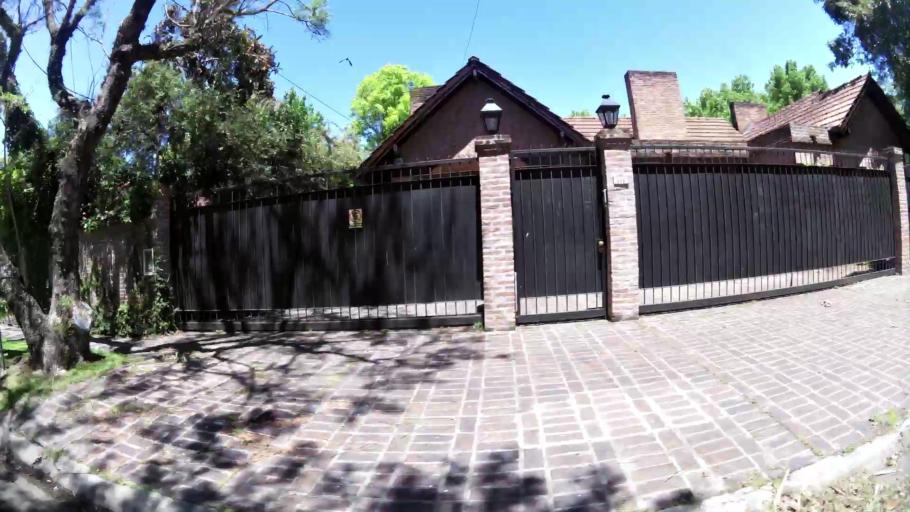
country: AR
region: Buenos Aires
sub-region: Partido de San Isidro
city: San Isidro
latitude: -34.5007
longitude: -58.5616
